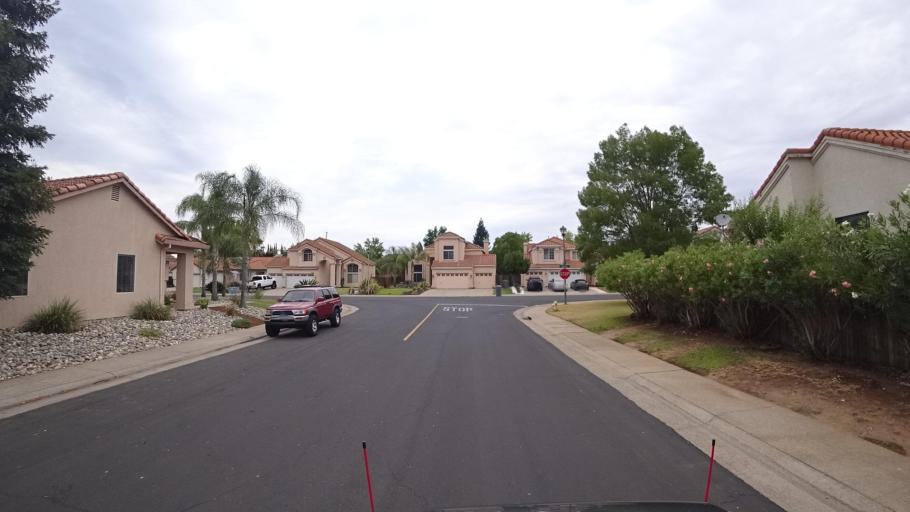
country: US
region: California
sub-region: Placer County
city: Rocklin
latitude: 38.7901
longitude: -121.2625
